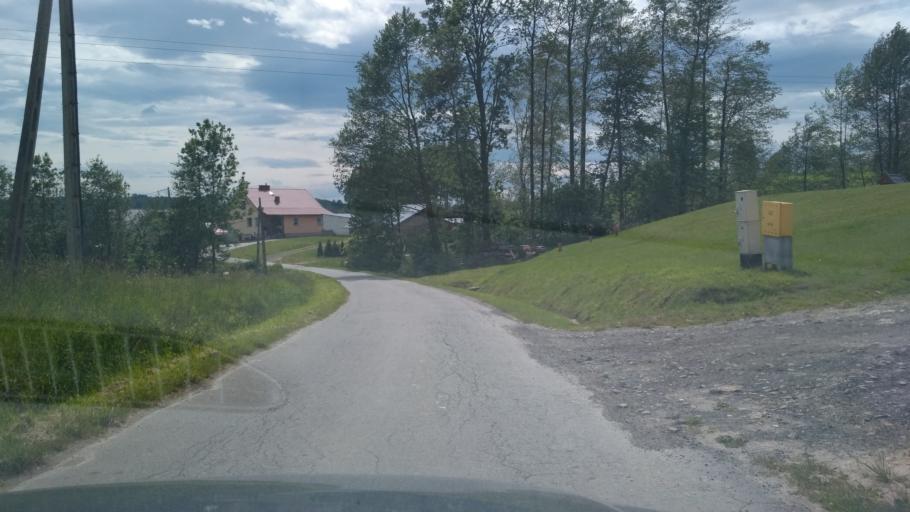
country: PL
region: Subcarpathian Voivodeship
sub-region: Powiat ropczycko-sedziszowski
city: Wielopole Skrzynskie
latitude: 49.9504
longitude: 21.6674
